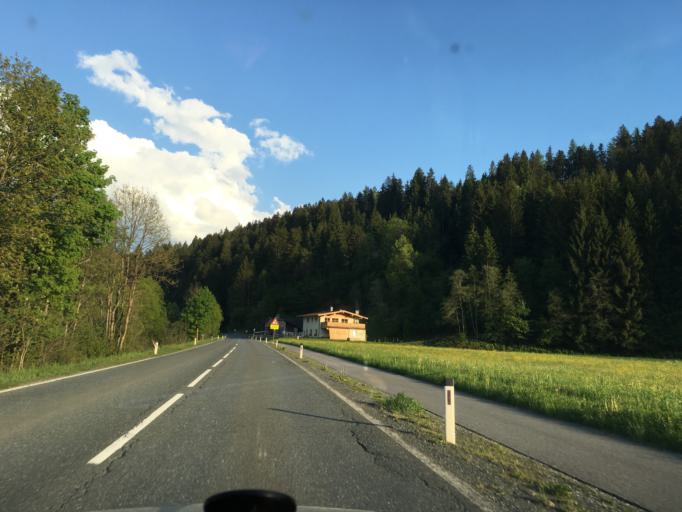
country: AT
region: Tyrol
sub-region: Politischer Bezirk Kitzbuhel
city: Fieberbrunn
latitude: 47.4985
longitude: 12.4887
